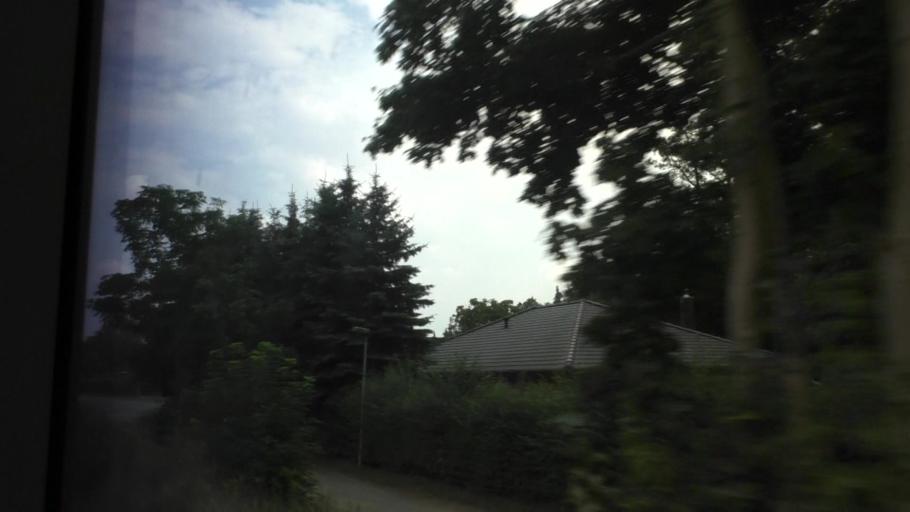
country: DE
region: Brandenburg
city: Konigs Wusterhausen
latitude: 52.3010
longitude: 13.6571
